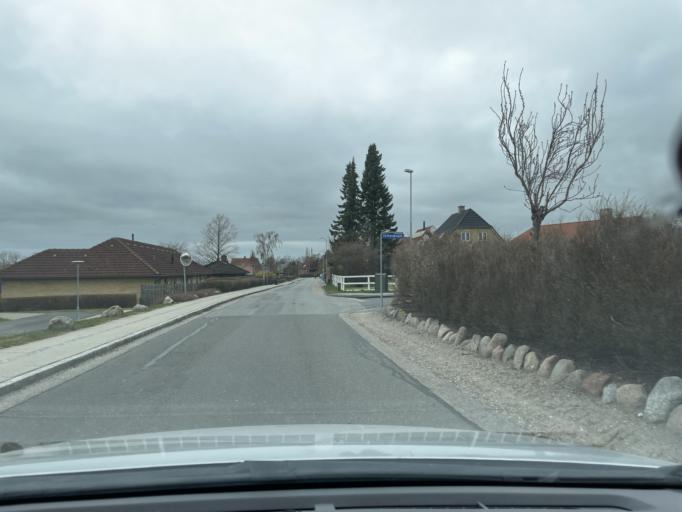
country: DK
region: South Denmark
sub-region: Nyborg Kommune
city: Nyborg
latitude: 55.3539
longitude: 10.7317
